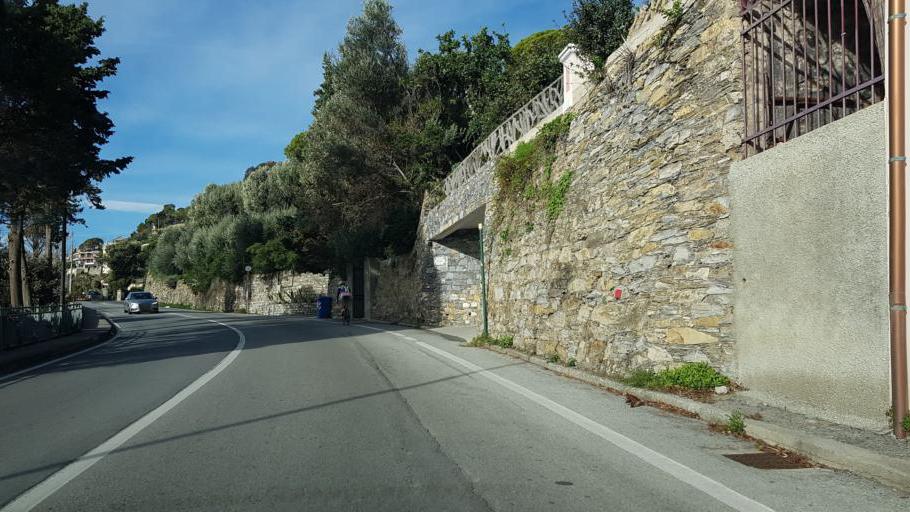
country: IT
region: Liguria
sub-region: Provincia di Genova
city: Recco
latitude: 44.3638
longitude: 9.1254
